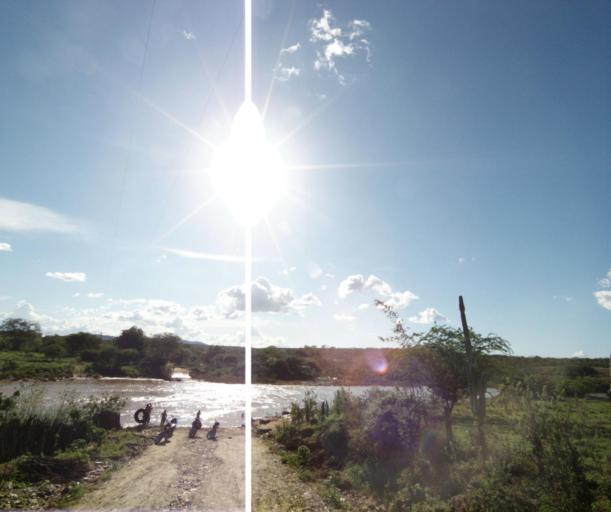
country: BR
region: Bahia
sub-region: Tanhacu
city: Tanhacu
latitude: -14.1827
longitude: -41.0148
